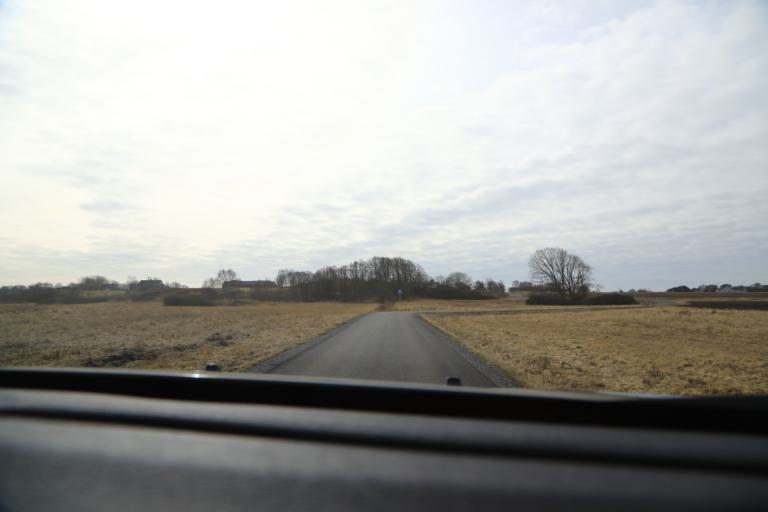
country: SE
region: Halland
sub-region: Kungsbacka Kommun
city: Frillesas
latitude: 57.2316
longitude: 12.1368
